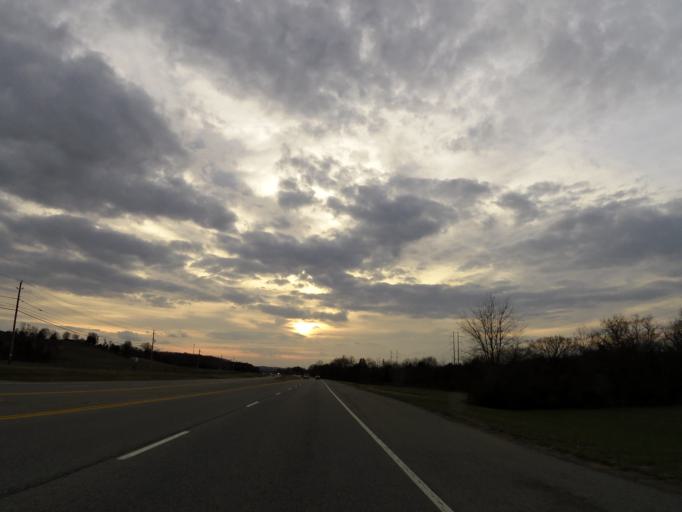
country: US
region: Tennessee
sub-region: Loudon County
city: Greenback
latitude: 35.6234
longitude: -84.1867
